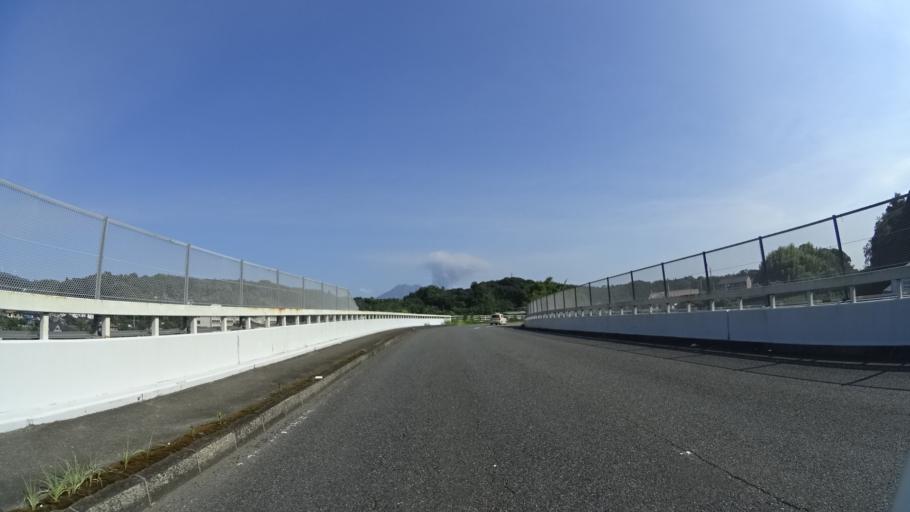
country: JP
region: Kagoshima
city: Kagoshima-shi
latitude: 31.6534
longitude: 130.5515
